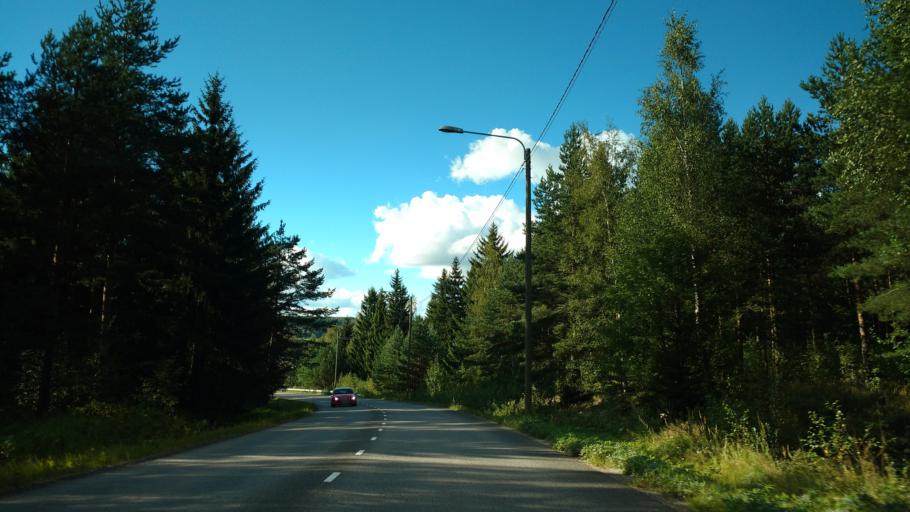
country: FI
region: Varsinais-Suomi
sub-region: Salo
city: Salo
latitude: 60.4009
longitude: 23.1748
